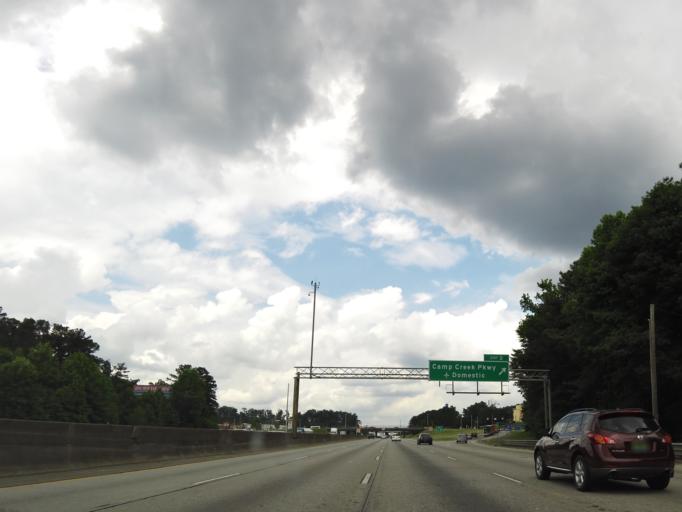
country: US
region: Georgia
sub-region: Fulton County
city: College Park
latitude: 33.6529
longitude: -84.4975
